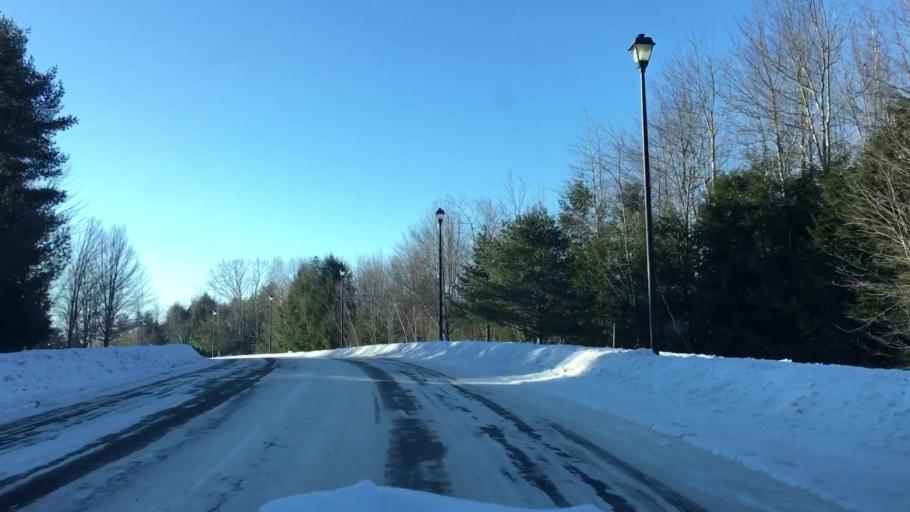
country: US
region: Maine
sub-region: Sagadahoc County
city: Topsham
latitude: 43.9388
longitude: -69.9561
